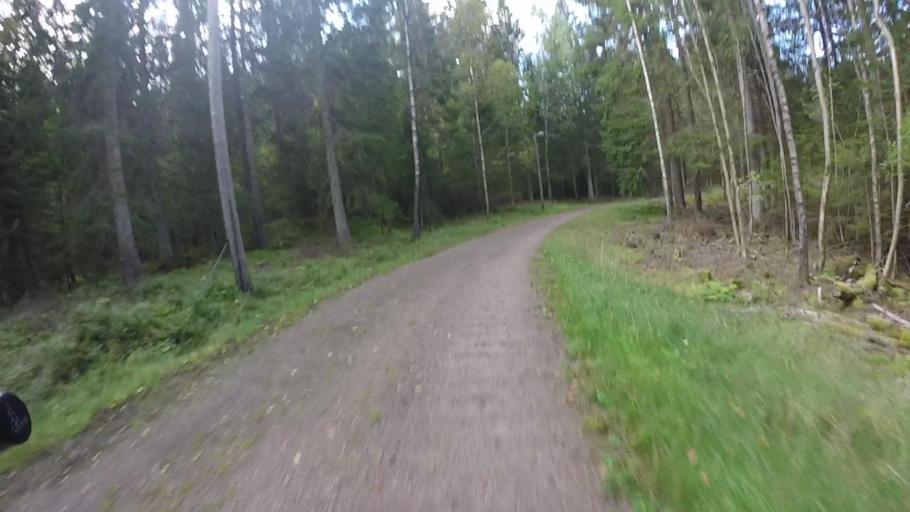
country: SE
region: Vaestra Goetaland
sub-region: Trollhattan
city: Trollhattan
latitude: 58.2496
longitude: 12.2493
